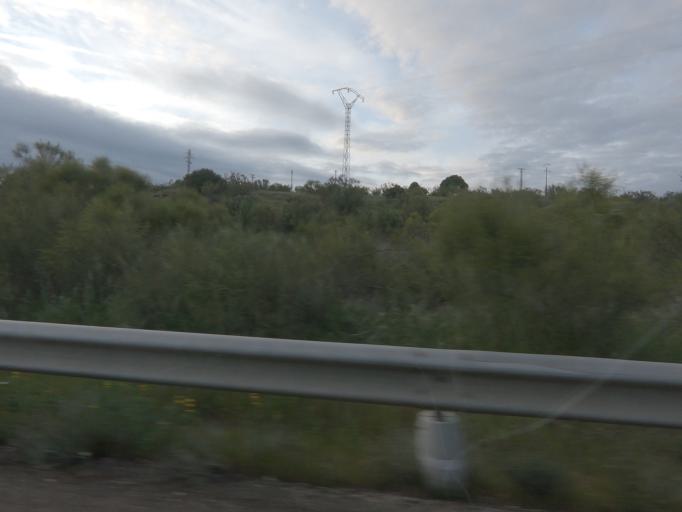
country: ES
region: Extremadura
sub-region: Provincia de Badajoz
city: La Roca de la Sierra
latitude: 39.1093
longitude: -6.6948
